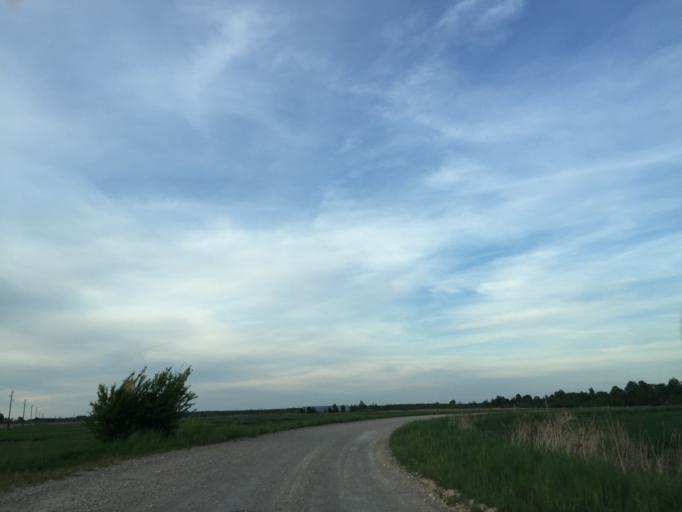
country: LV
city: Tireli
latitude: 56.8000
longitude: 23.5712
